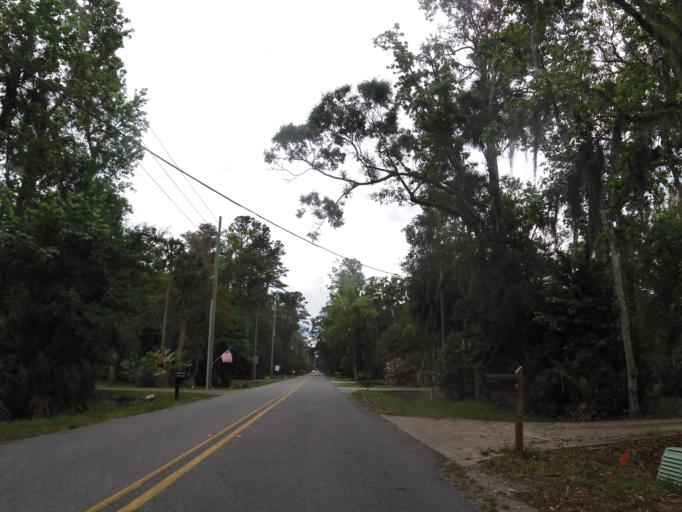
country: US
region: Florida
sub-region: Saint Johns County
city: Palm Valley
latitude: 30.1922
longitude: -81.4042
